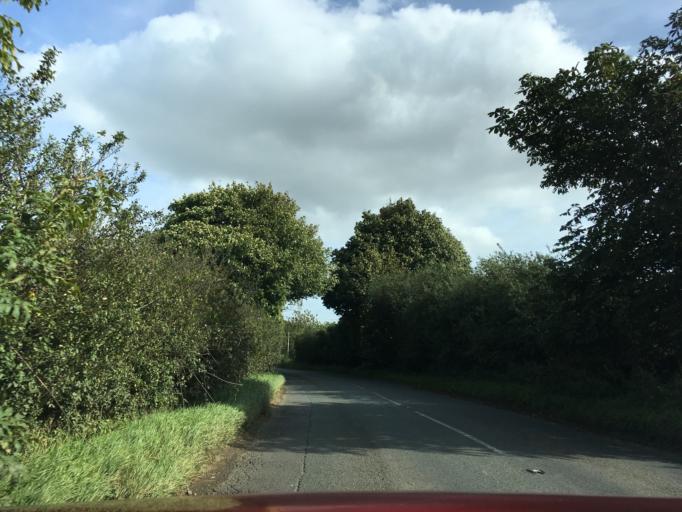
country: GB
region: England
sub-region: Gloucestershire
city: Stonehouse
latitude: 51.6915
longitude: -2.2815
